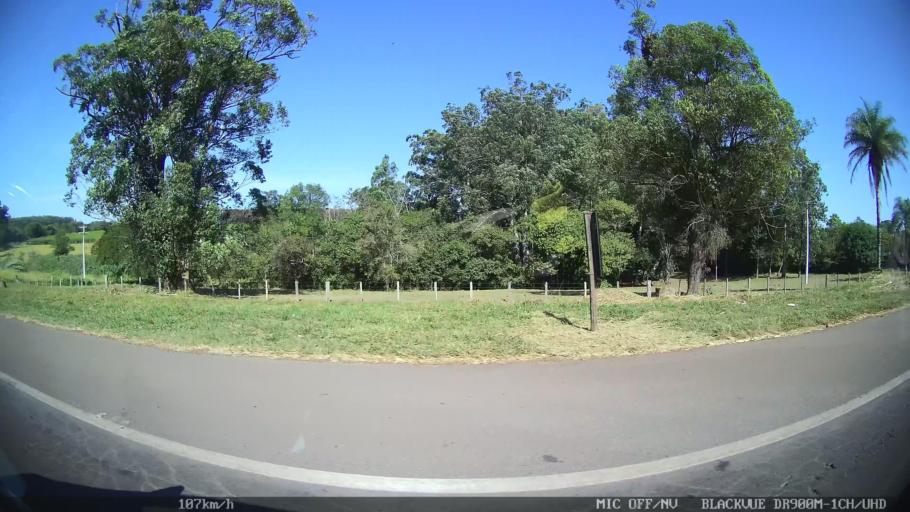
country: BR
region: Sao Paulo
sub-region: Batatais
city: Batatais
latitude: -20.9092
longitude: -47.5936
